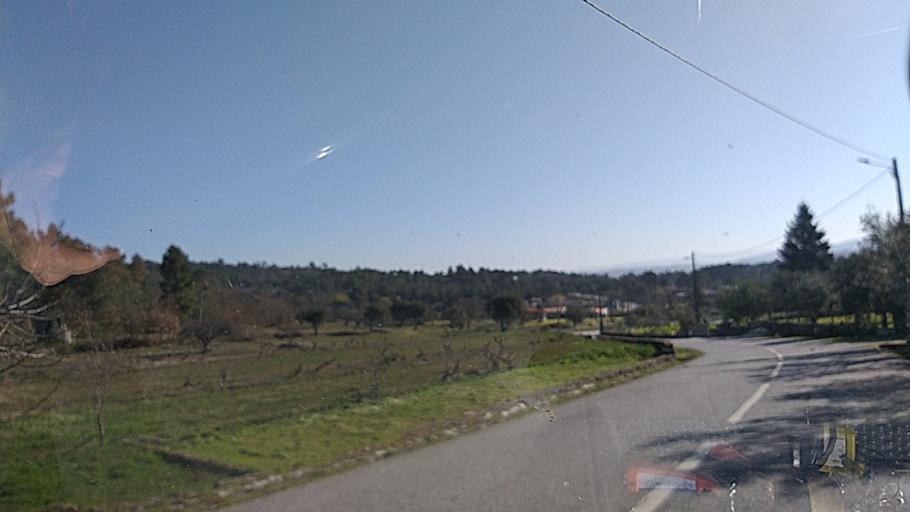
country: PT
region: Guarda
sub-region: Fornos de Algodres
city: Fornos de Algodres
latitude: 40.6333
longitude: -7.4957
